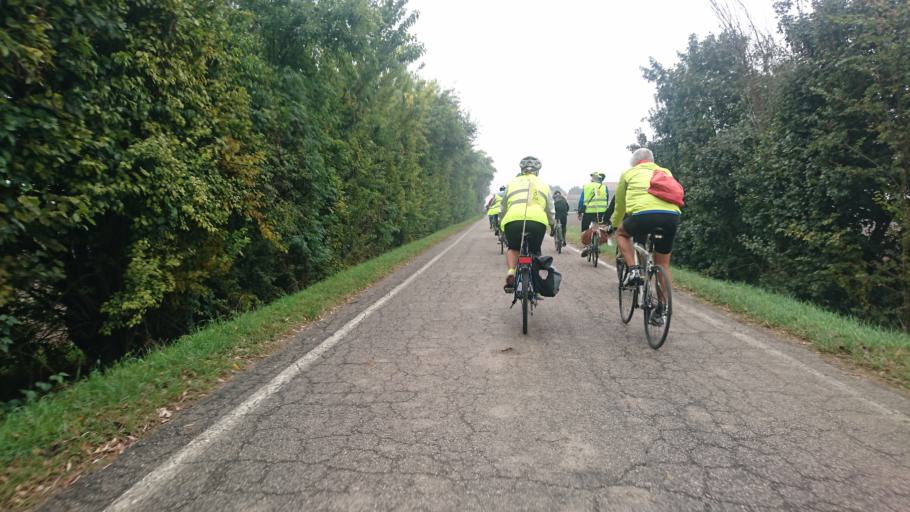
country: IT
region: Veneto
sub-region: Provincia di Padova
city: Pozzonovo
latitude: 45.1628
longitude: 11.7879
